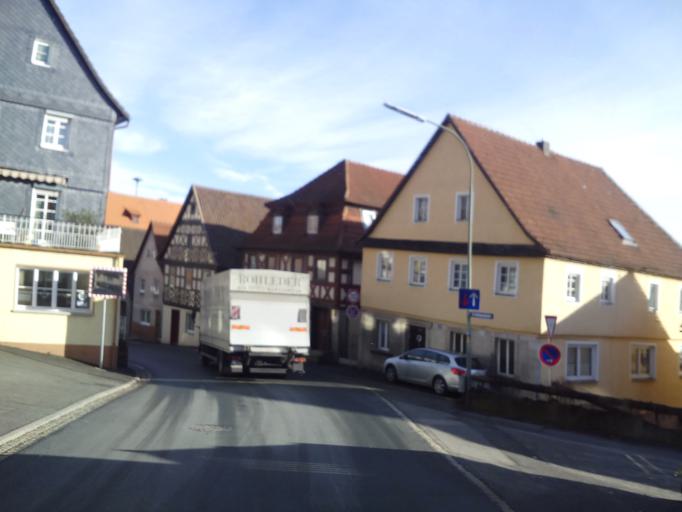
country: DE
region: Bavaria
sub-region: Upper Franconia
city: Marktzeuln
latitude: 50.1664
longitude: 11.1683
